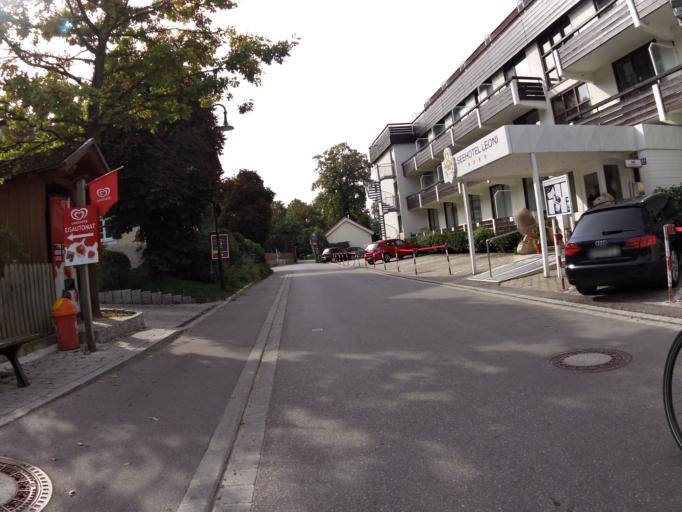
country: DE
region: Bavaria
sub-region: Upper Bavaria
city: Berg
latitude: 47.9556
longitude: 11.3439
